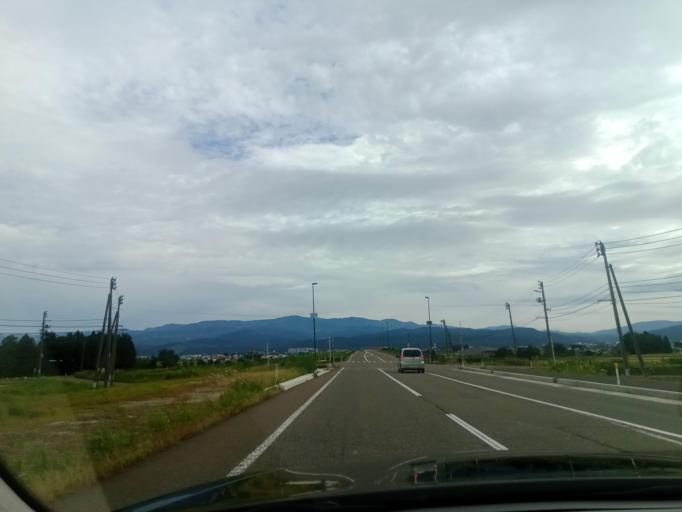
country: JP
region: Niigata
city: Arai
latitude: 37.0694
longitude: 138.2405
